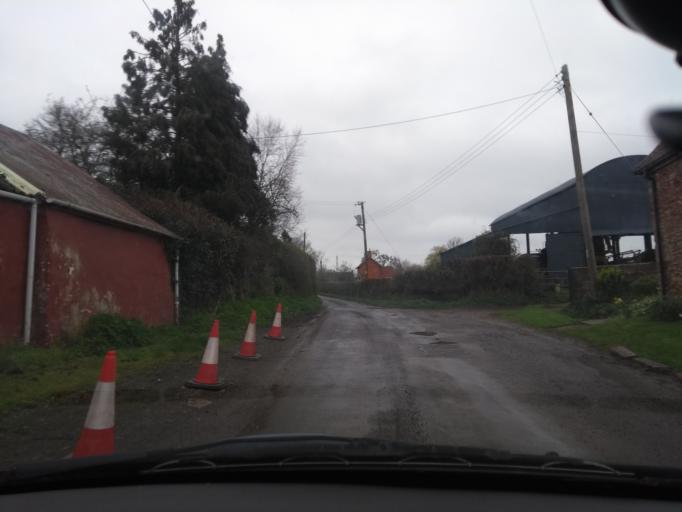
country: GB
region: England
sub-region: Somerset
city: Taunton
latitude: 51.0366
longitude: -3.1164
